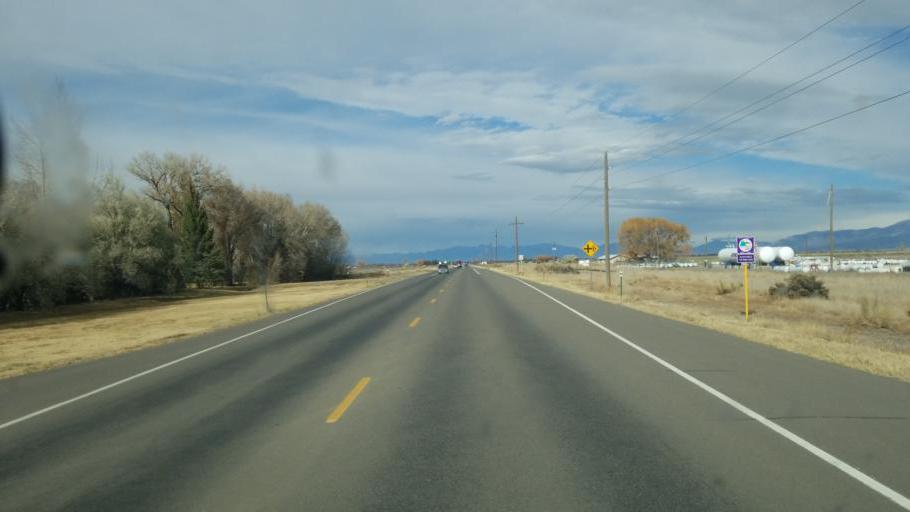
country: US
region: Colorado
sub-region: Alamosa County
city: Alamosa
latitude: 37.3985
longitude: -105.9074
